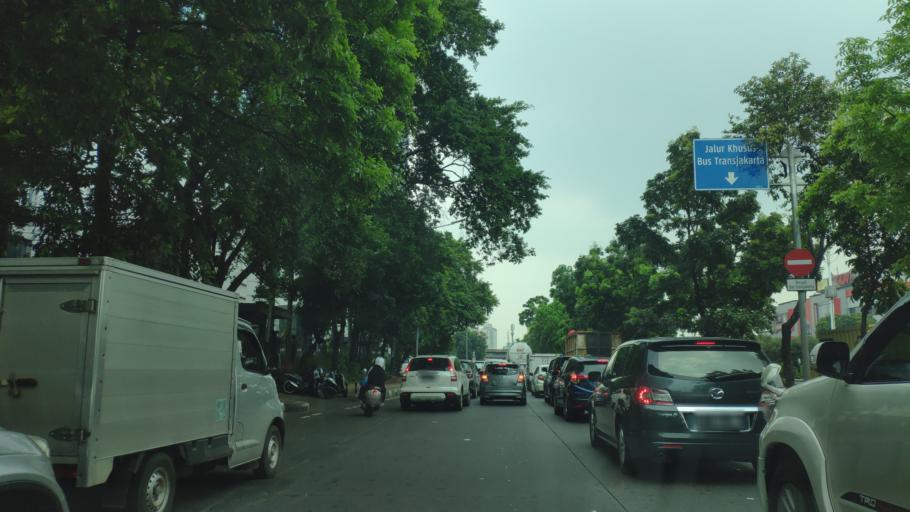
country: ID
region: Jakarta Raya
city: Jakarta
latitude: -6.1875
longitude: 106.7972
